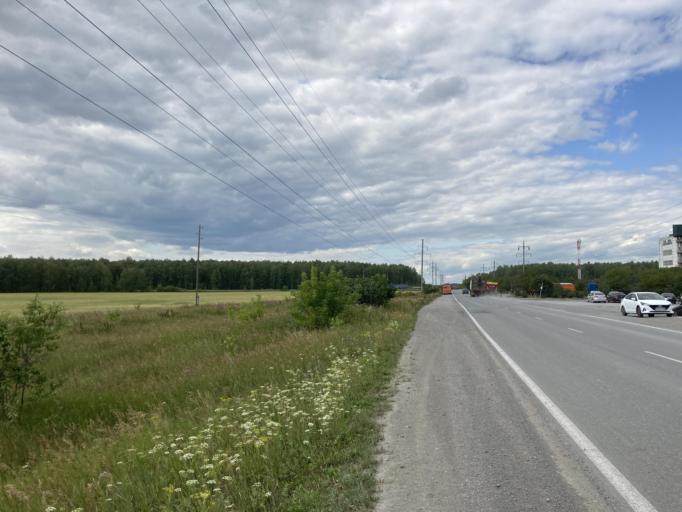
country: RU
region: Sverdlovsk
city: Bogdanovich
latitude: 56.8039
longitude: 62.0359
